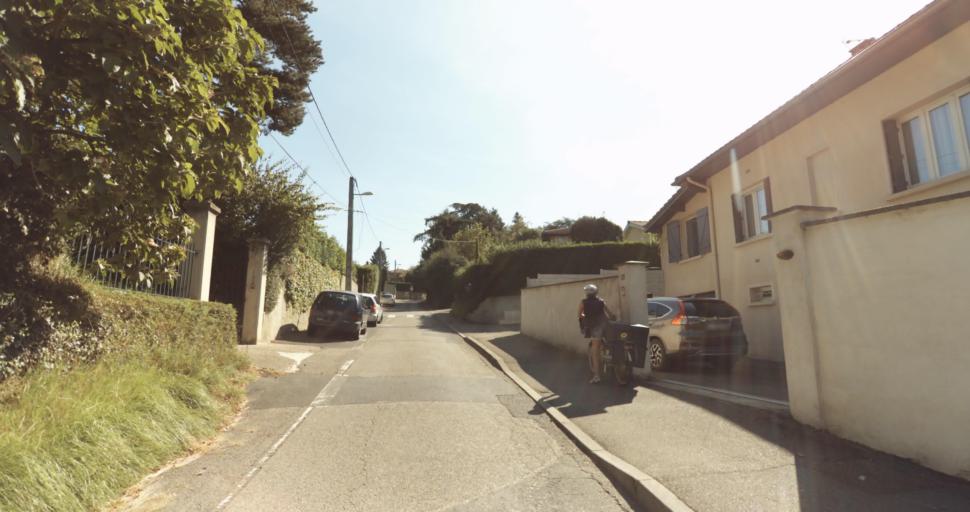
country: FR
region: Rhone-Alpes
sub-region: Departement du Rhone
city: Neuville-sur-Saone
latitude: 45.8748
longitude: 4.8471
